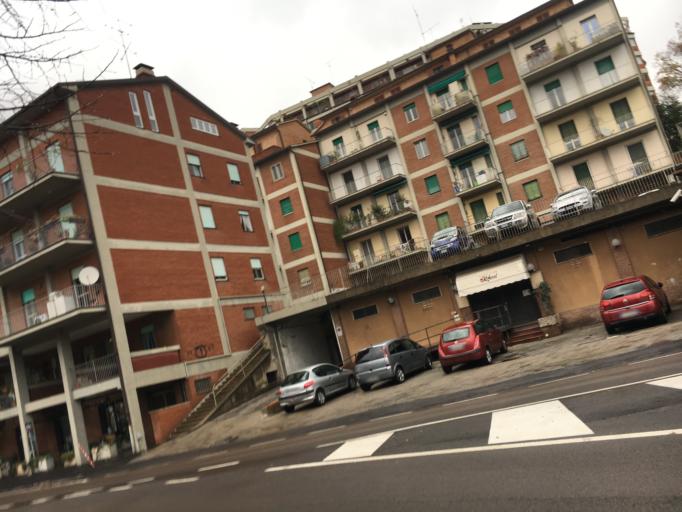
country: IT
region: Umbria
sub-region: Provincia di Perugia
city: Perugia
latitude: 43.1143
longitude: 12.3765
